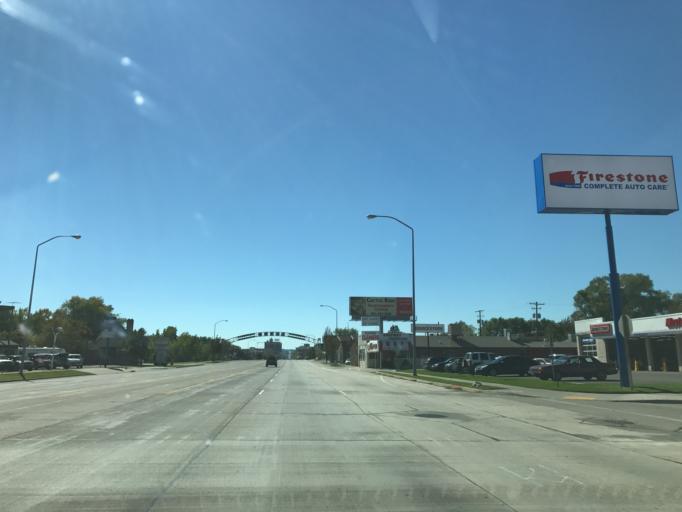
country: US
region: Utah
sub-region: Weber County
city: Ogden
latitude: 41.2359
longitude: -111.9702
